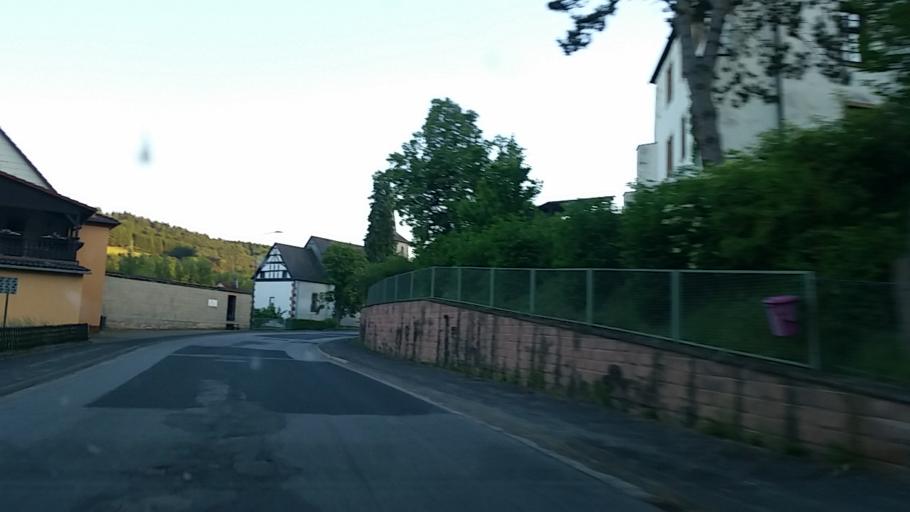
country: DE
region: Bavaria
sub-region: Regierungsbezirk Unterfranken
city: Obersinn
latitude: 50.2522
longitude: 9.6205
